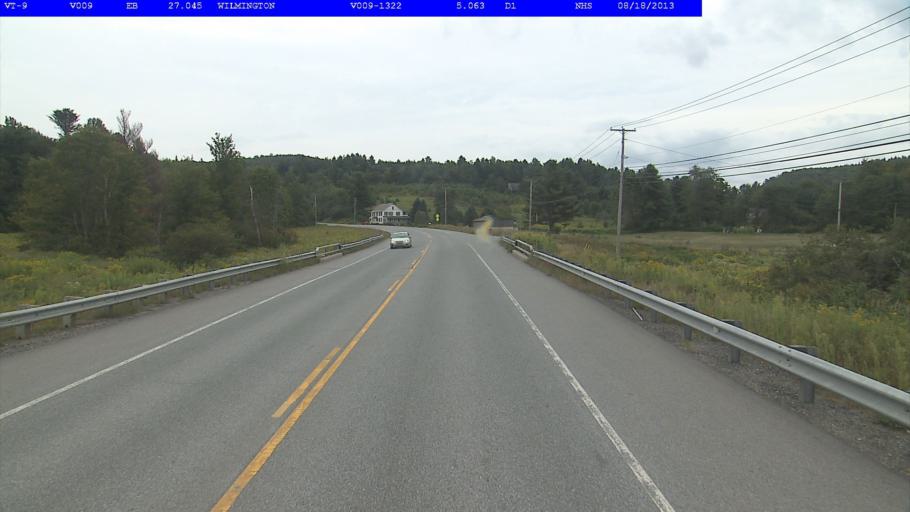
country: US
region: Vermont
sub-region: Windham County
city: Dover
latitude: 42.8556
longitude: -72.8381
